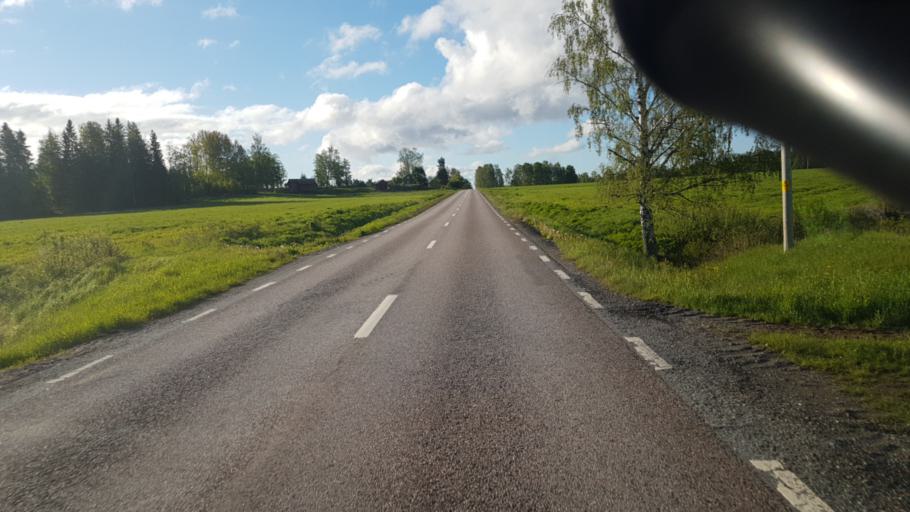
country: SE
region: Vaermland
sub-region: Arvika Kommun
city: Arvika
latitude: 59.6143
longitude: 12.5171
